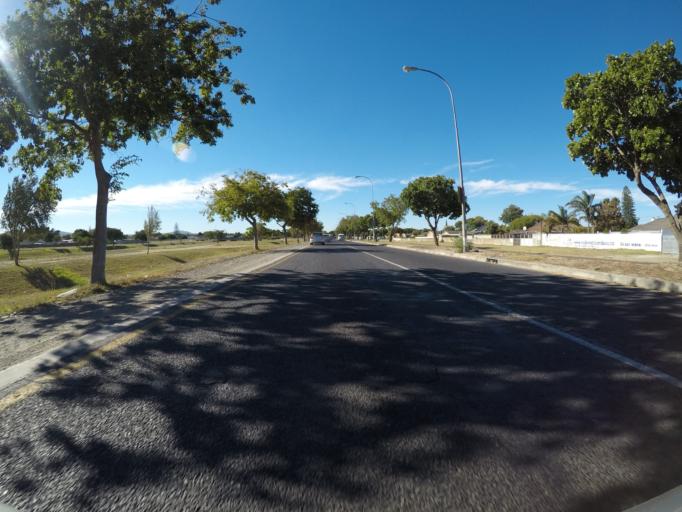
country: ZA
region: Western Cape
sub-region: City of Cape Town
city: Kraaifontein
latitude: -33.9292
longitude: 18.6767
